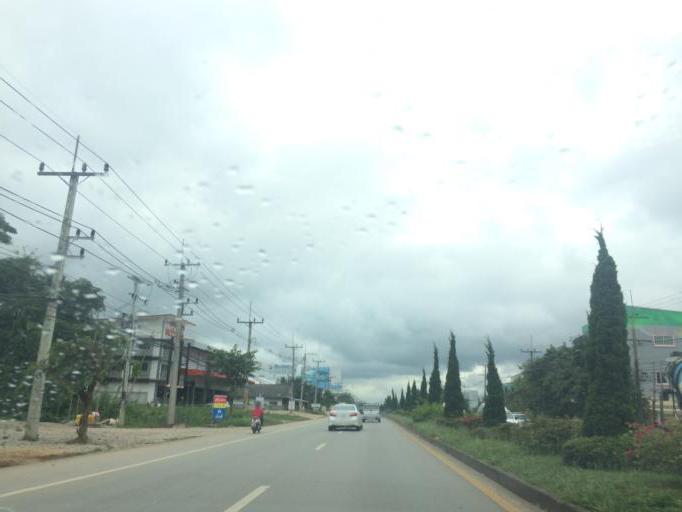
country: TH
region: Chiang Rai
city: Chiang Rai
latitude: 20.0096
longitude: 99.8683
